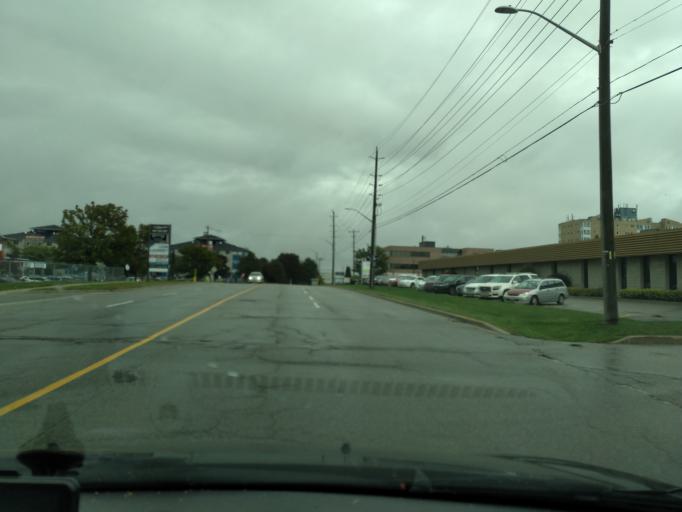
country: CA
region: Ontario
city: Barrie
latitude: 44.4102
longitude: -79.6773
